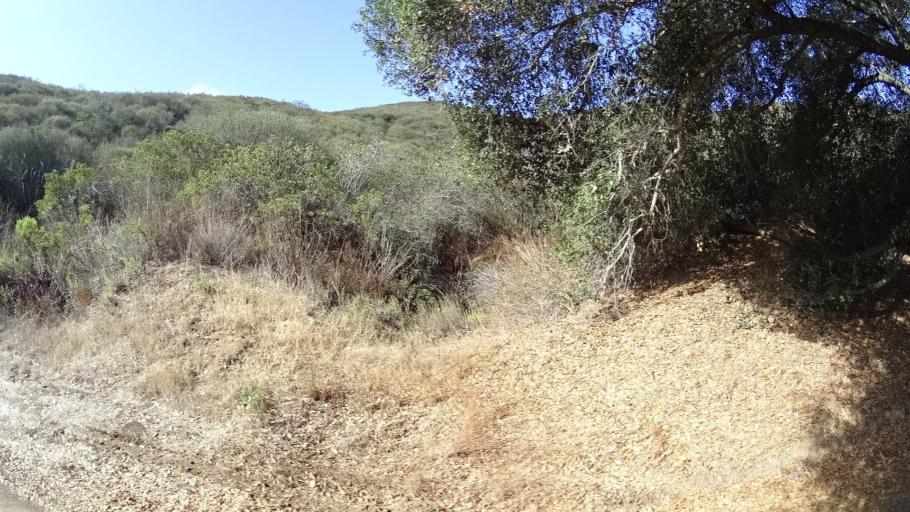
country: US
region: California
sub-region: San Diego County
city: Lake San Marcos
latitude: 33.0926
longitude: -117.1703
